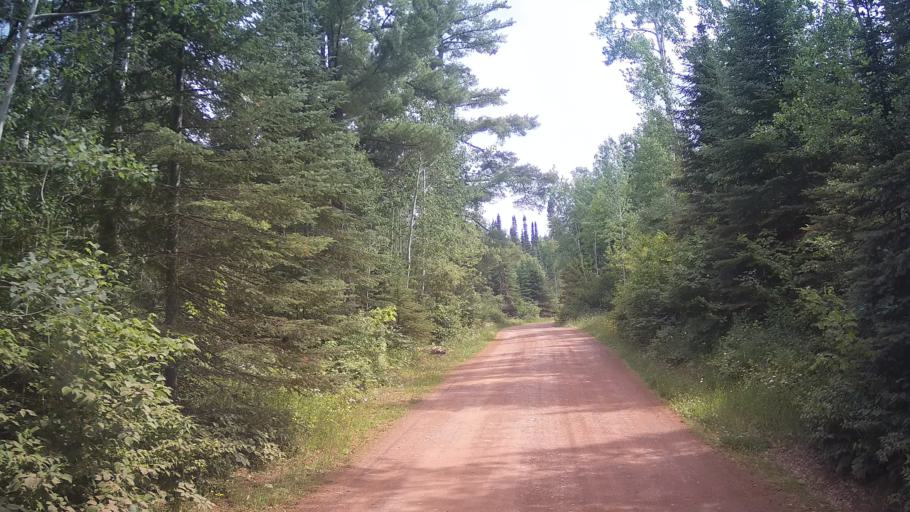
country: CA
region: Ontario
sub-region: Thunder Bay District
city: Thunder Bay
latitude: 48.6818
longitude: -88.6643
